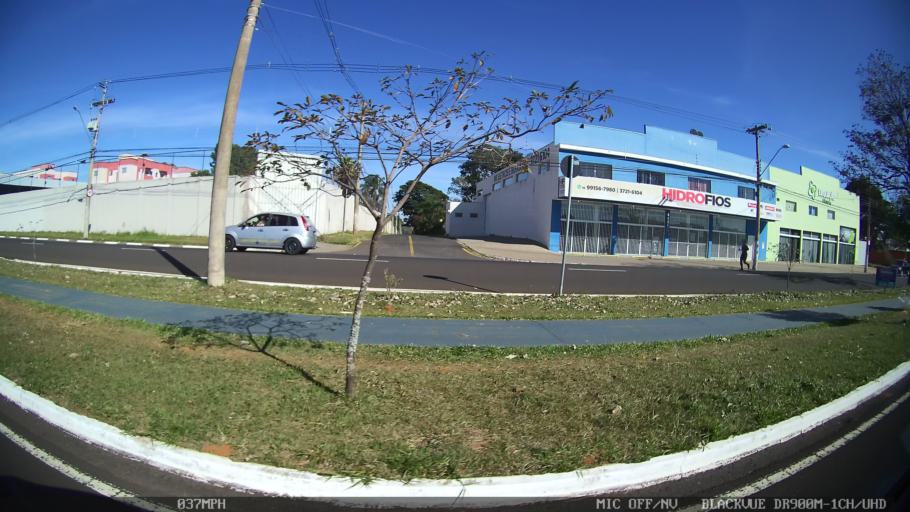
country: BR
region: Sao Paulo
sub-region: Franca
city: Franca
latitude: -20.5575
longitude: -47.3597
